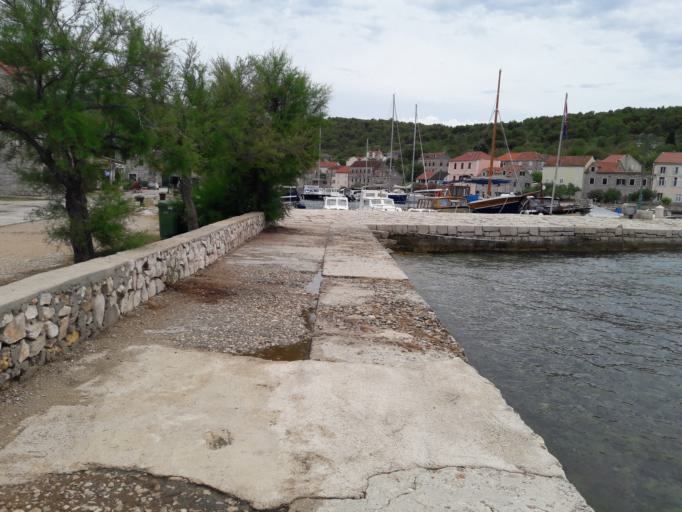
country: HR
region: Sibensko-Kniniska
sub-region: Grad Sibenik
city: Sibenik
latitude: 43.6987
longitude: 15.8345
